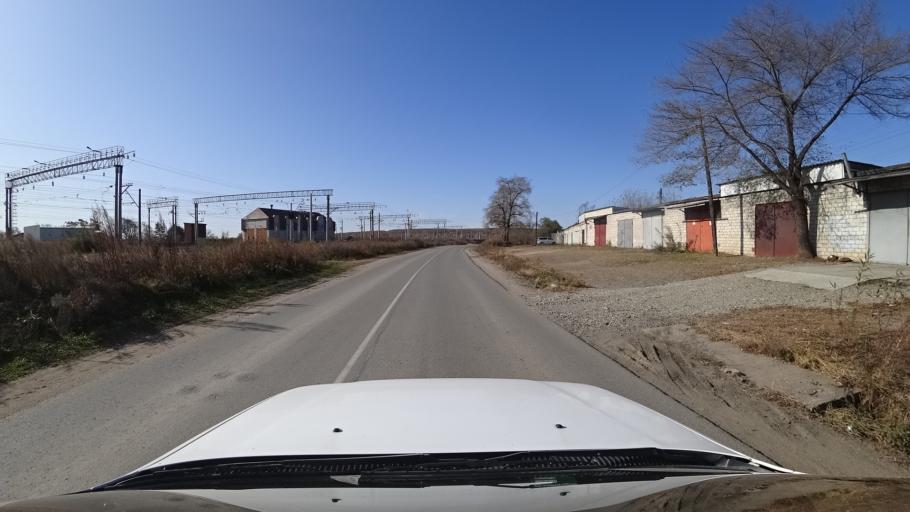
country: RU
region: Primorskiy
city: Dal'nerechensk
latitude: 45.9342
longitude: 133.7181
